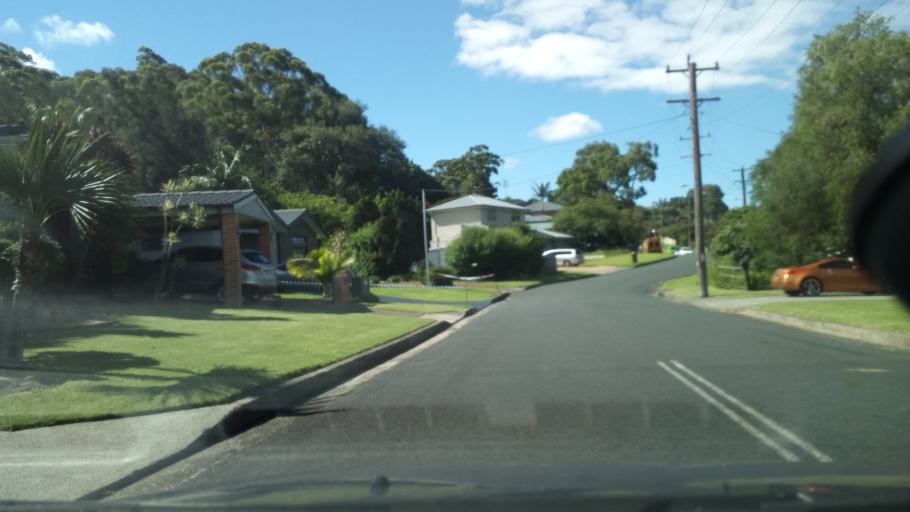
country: AU
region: New South Wales
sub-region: Wollongong
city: Mount Ousley
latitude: -34.3998
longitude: 150.8769
